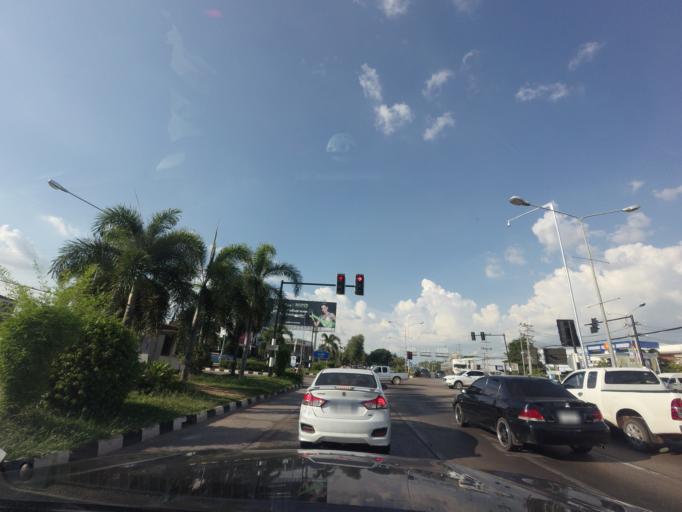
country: TH
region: Khon Kaen
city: Ban Phai
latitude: 16.0573
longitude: 102.7159
